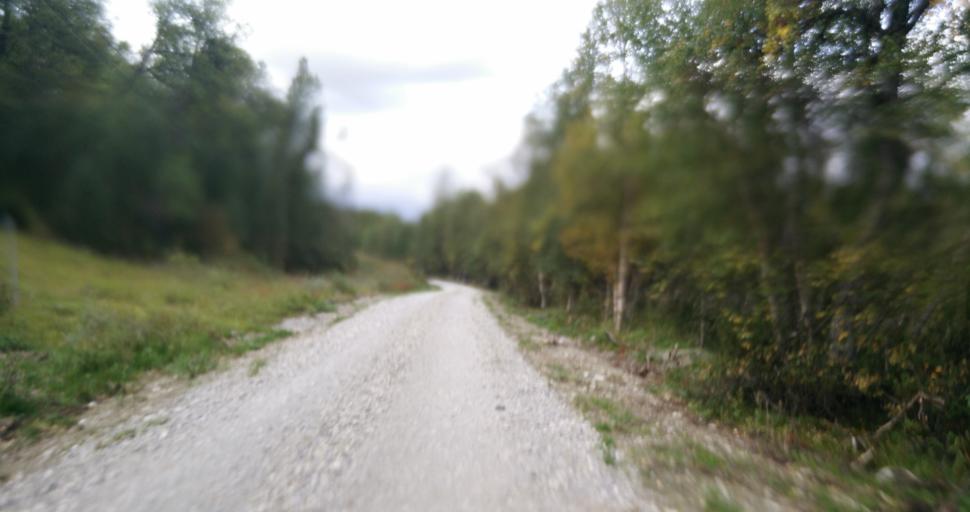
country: NO
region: Sor-Trondelag
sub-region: Tydal
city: Aas
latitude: 62.6372
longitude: 12.4183
